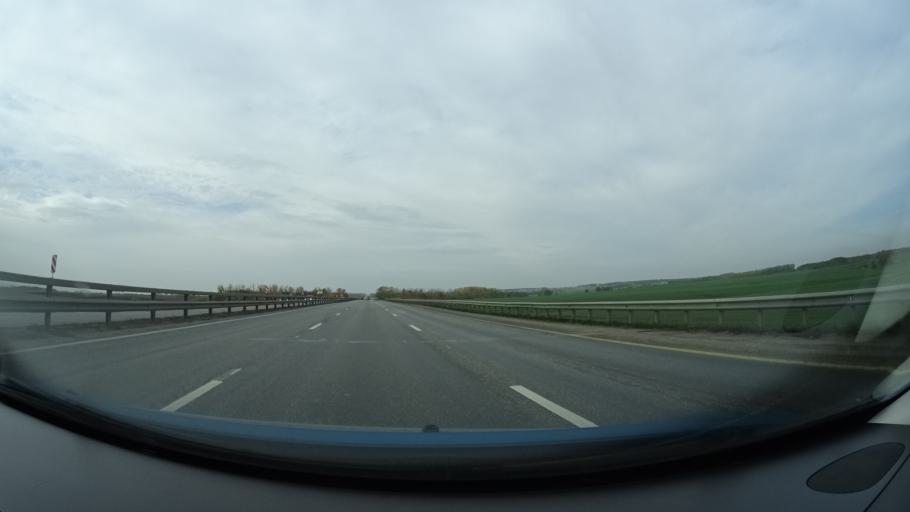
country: RU
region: Bashkortostan
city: Avdon
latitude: 54.6714
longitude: 55.7707
